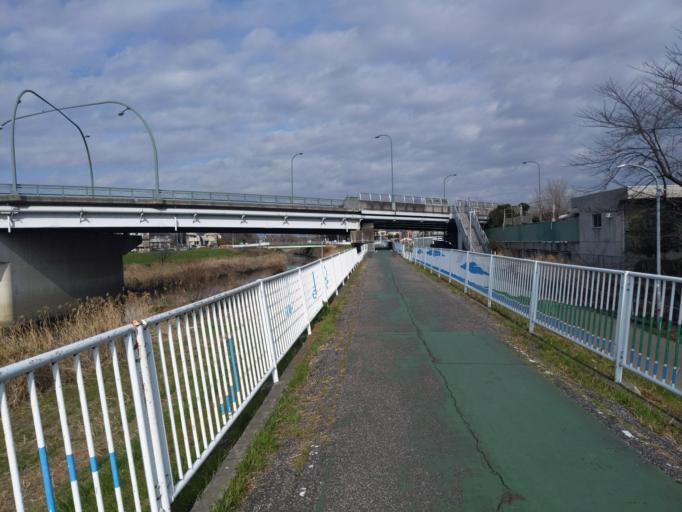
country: JP
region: Saitama
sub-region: Kawaguchi-shi
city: Hatogaya-honcho
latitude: 35.8598
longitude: 139.7134
